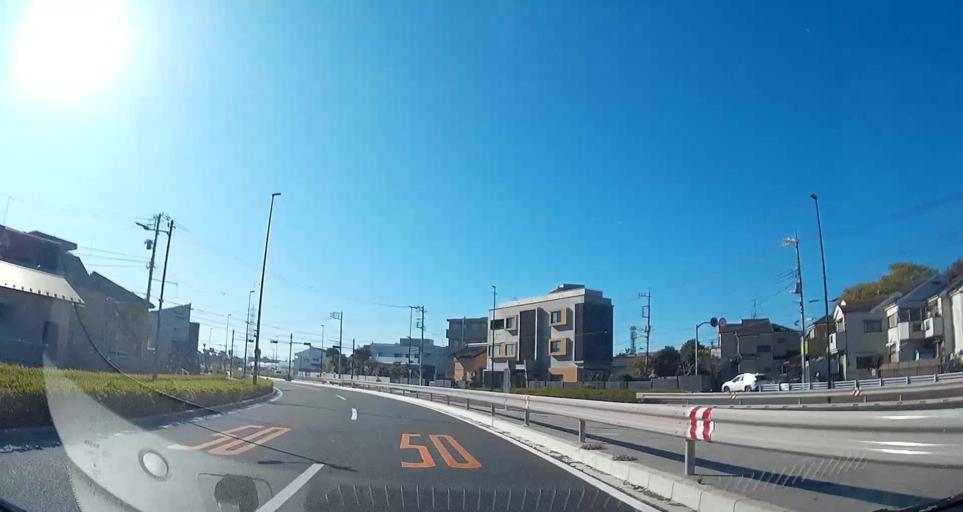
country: JP
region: Tokyo
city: Mitaka-shi
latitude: 35.6855
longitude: 139.5911
